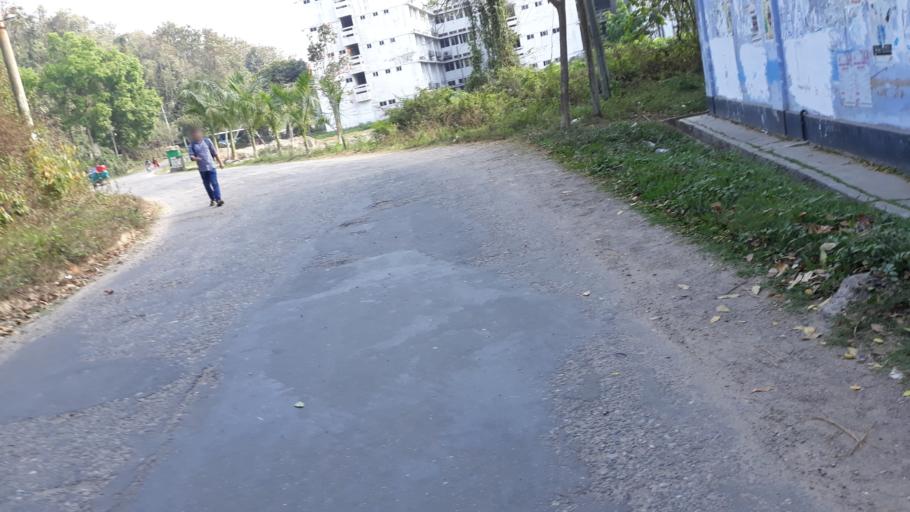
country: BD
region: Chittagong
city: Chittagong
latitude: 22.4686
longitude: 91.7808
